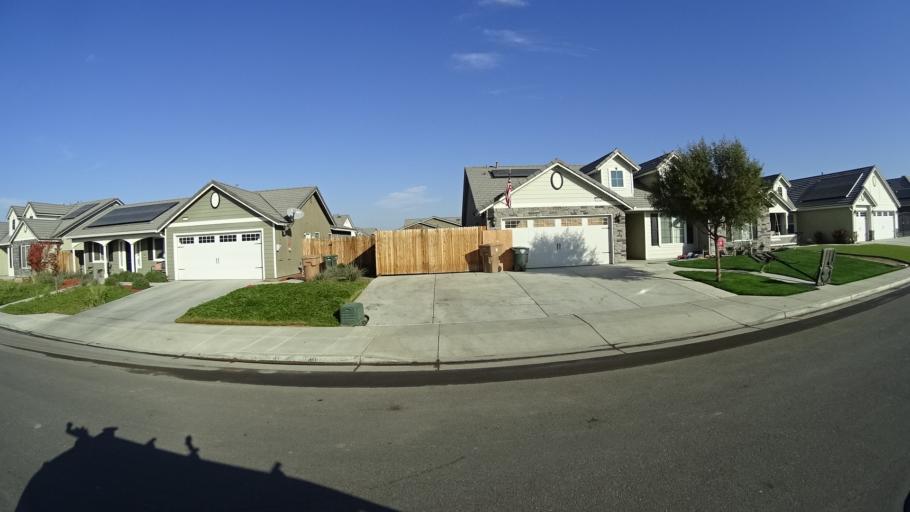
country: US
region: California
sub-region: Kern County
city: Greenfield
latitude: 35.2729
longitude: -119.0703
